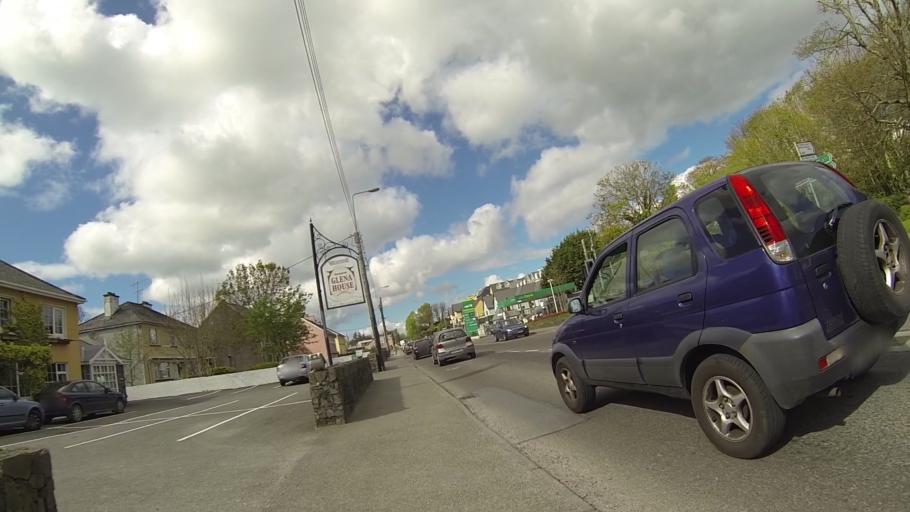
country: IE
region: Munster
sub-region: Ciarrai
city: Cill Airne
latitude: 52.0522
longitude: -9.5068
